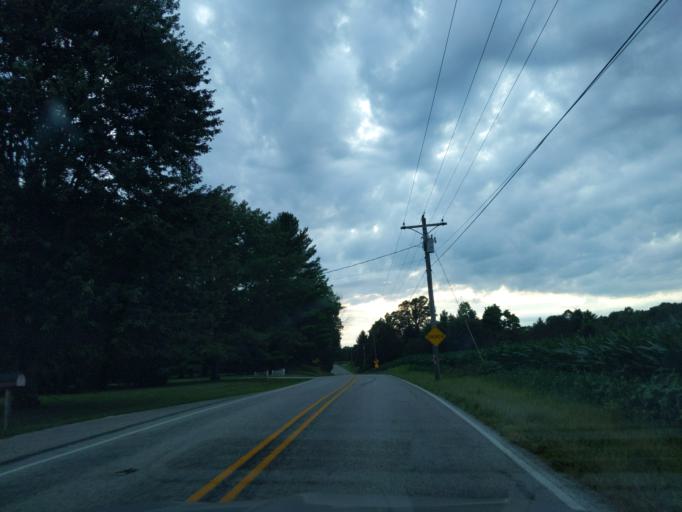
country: US
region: Indiana
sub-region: Ripley County
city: Osgood
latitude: 39.1972
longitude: -85.2405
